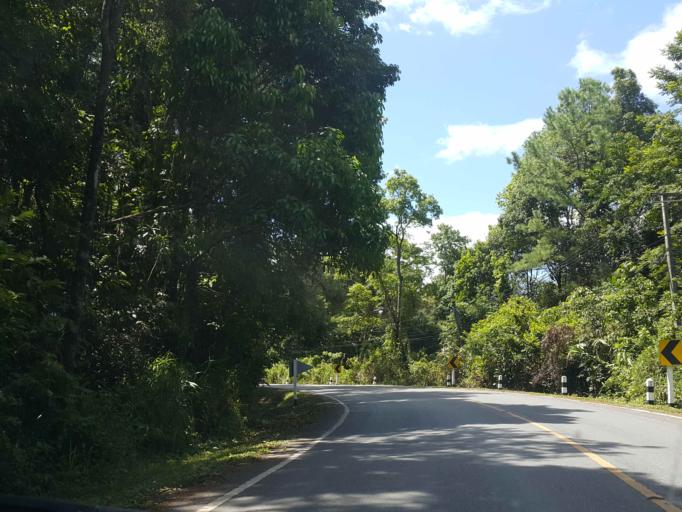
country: TH
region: Chiang Mai
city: Chom Thong
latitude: 18.5407
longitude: 98.5696
